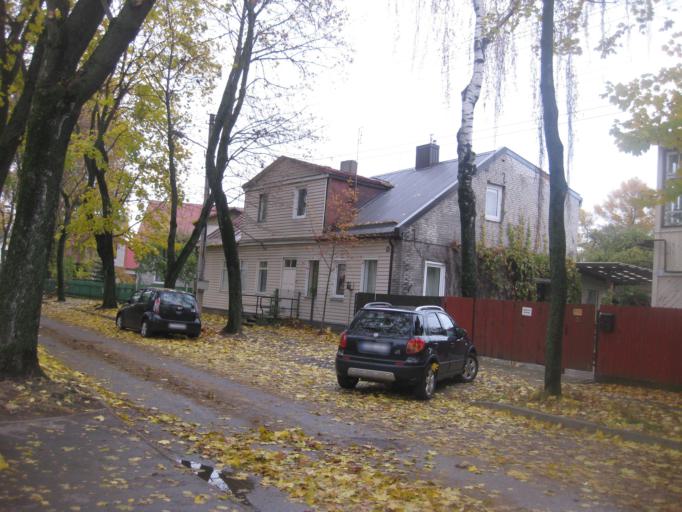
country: LT
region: Kauno apskritis
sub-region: Kaunas
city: Eiguliai
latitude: 54.9106
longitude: 23.9219
